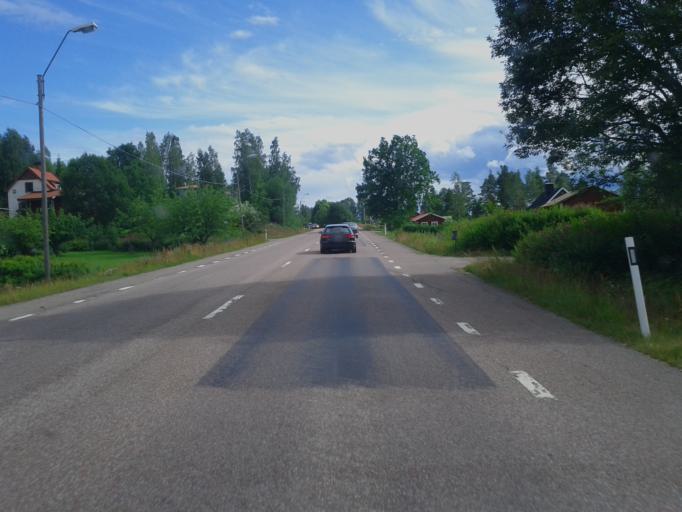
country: SE
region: Dalarna
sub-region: Faluns Kommun
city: Grycksbo
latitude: 60.6981
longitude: 15.4808
